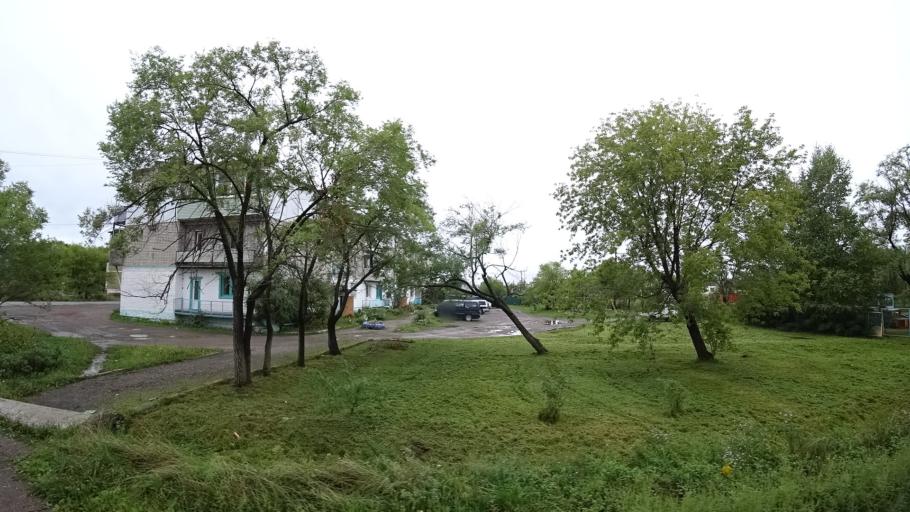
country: RU
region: Primorskiy
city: Monastyrishche
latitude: 44.2009
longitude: 132.4955
